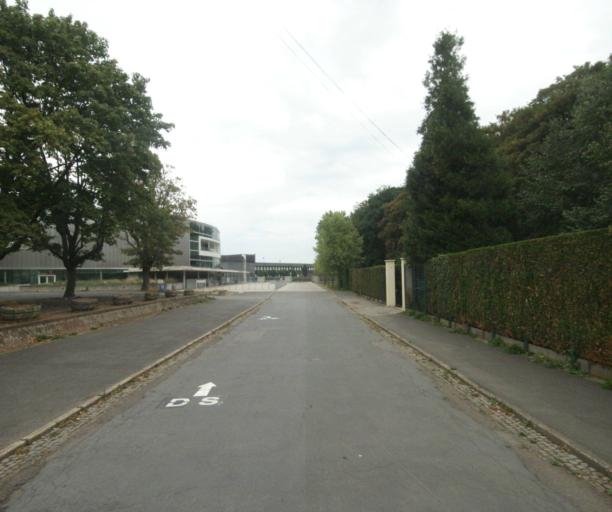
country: FR
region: Nord-Pas-de-Calais
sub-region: Departement du Nord
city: Lannoy
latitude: 50.6788
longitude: 3.2048
